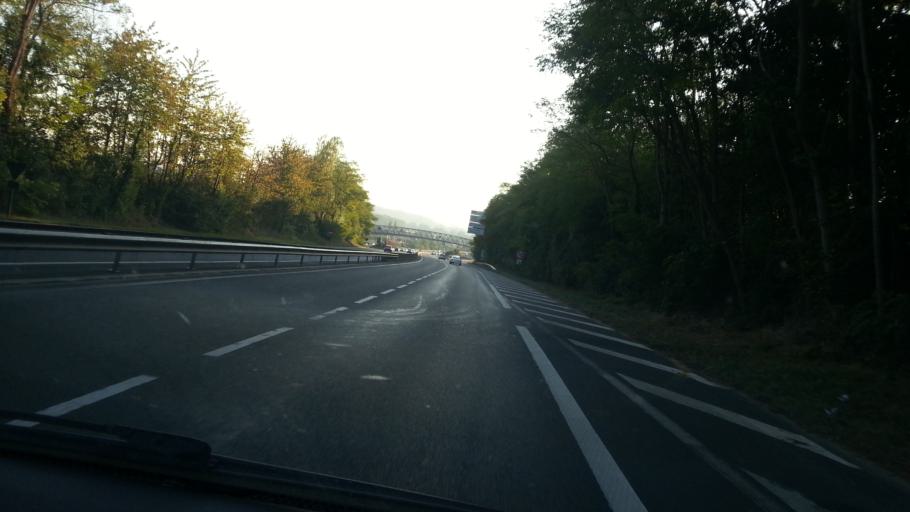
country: FR
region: Picardie
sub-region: Departement de l'Oise
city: Rieux
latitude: 49.3032
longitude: 2.5243
